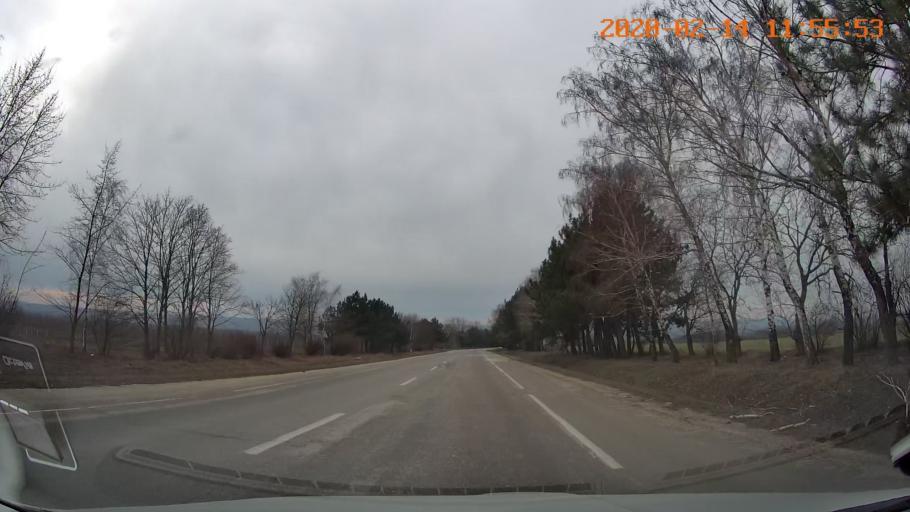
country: RO
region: Botosani
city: Radauti
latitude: 48.2750
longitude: 26.8294
